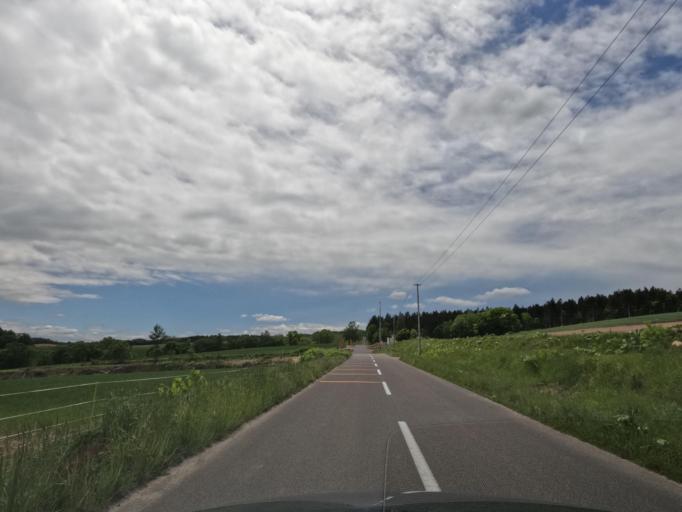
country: JP
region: Hokkaido
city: Shimo-furano
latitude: 43.5012
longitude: 142.4134
